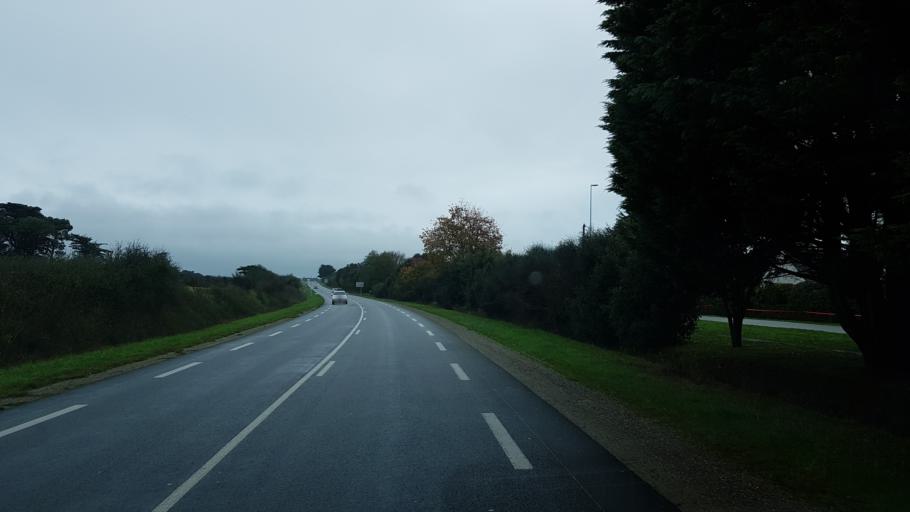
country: FR
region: Brittany
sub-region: Departement du Morbihan
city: Arzon
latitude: 47.5401
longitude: -2.8769
